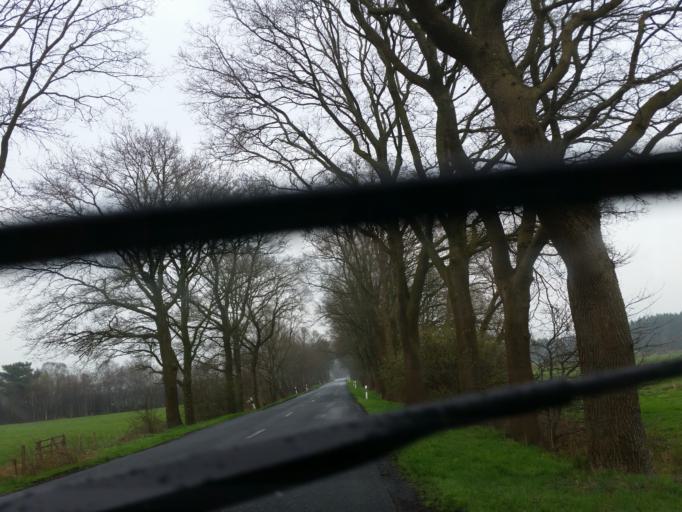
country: DE
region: Lower Saxony
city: Hipstedt
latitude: 53.5603
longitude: 8.9826
